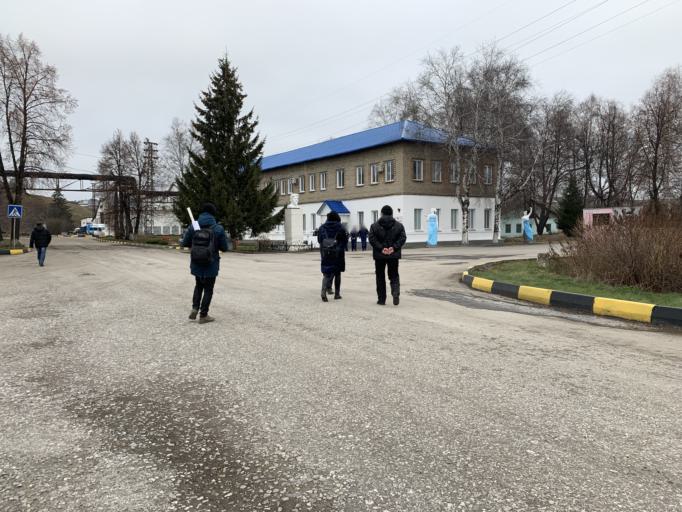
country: RU
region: Chelyabinsk
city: Nyazepetrovsk
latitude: 56.0535
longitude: 59.5900
